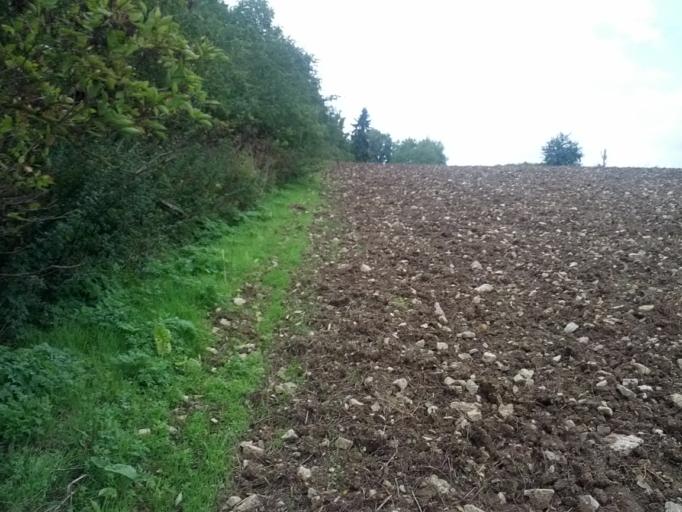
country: DE
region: Thuringia
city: Eisenach
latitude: 51.0123
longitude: 10.3229
